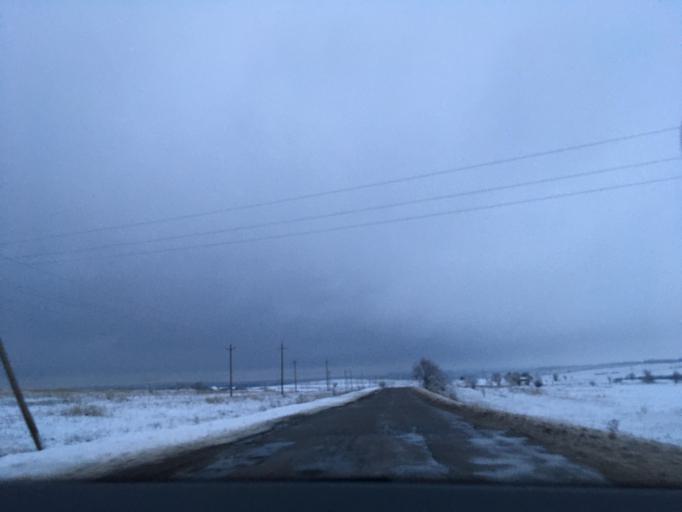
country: RU
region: Voronezj
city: Verkhniy Mamon
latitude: 50.0726
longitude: 40.2985
